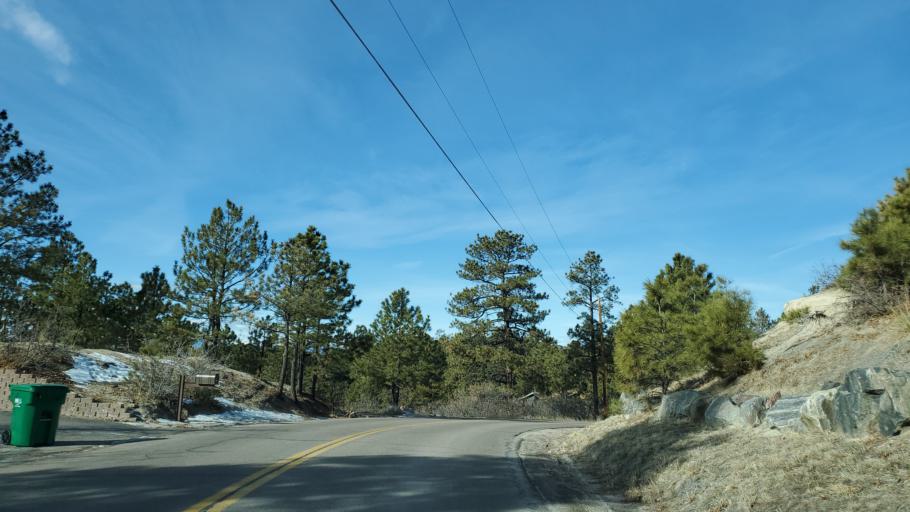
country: US
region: Colorado
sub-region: Douglas County
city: Castle Pines
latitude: 39.4352
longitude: -104.8727
